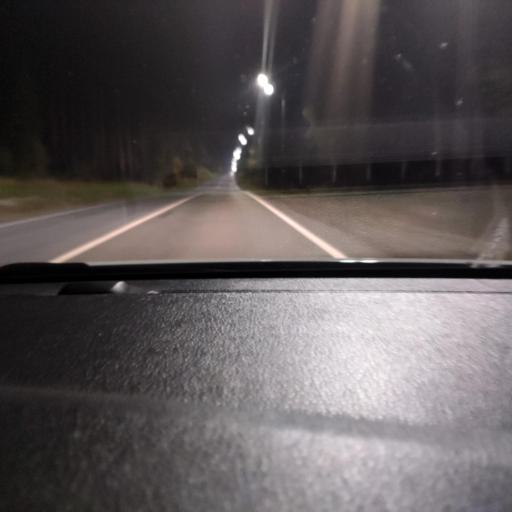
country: RU
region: Tatarstan
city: Verkhniy Uslon
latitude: 55.6374
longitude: 49.0527
